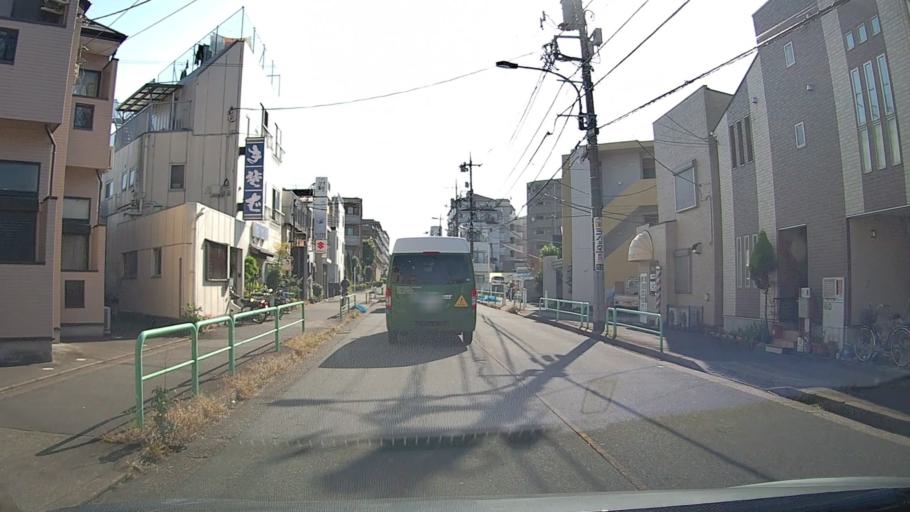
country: JP
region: Saitama
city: Wako
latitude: 35.7429
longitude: 139.6358
